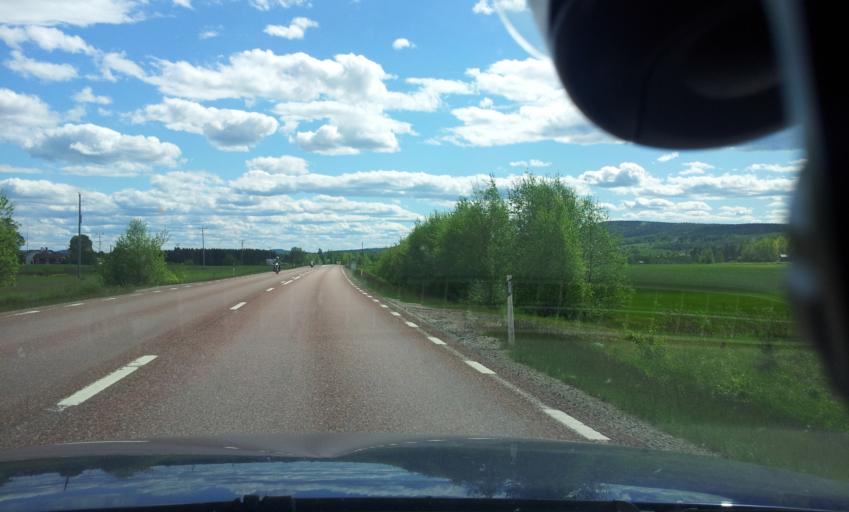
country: SE
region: Gaevleborg
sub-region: Bollnas Kommun
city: Arbra
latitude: 61.5339
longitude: 16.3638
